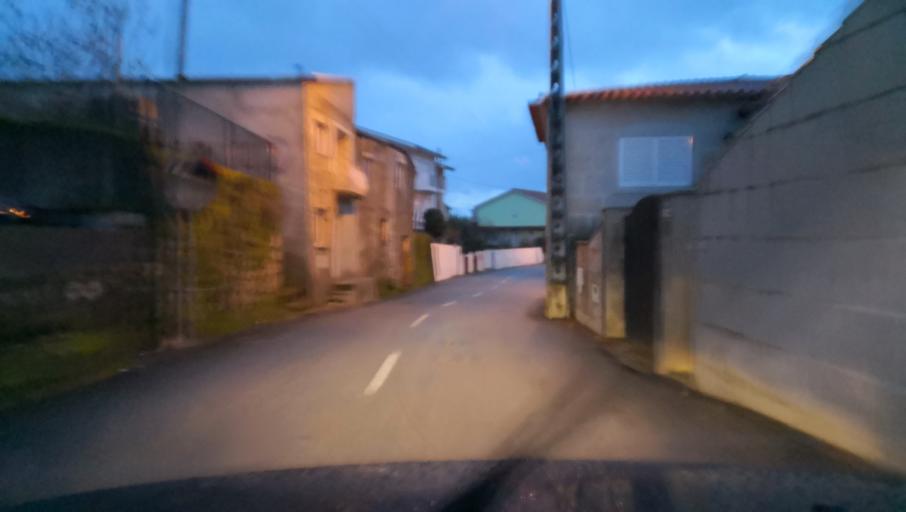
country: PT
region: Vila Real
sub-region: Vila Real
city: Vila Real
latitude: 41.3021
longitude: -7.7109
